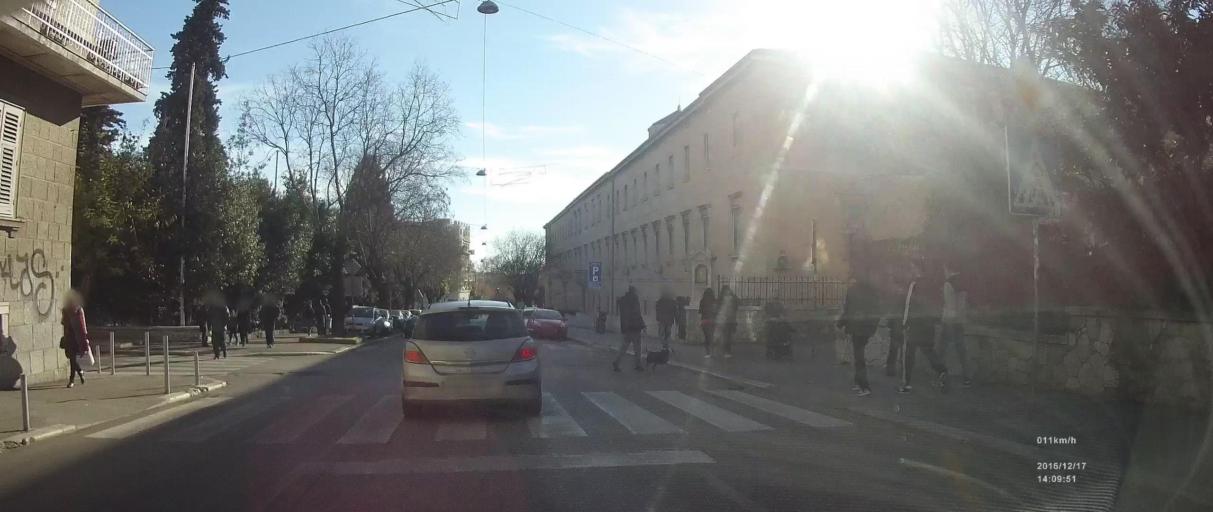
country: HR
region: Splitsko-Dalmatinska
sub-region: Grad Split
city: Split
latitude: 43.5149
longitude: 16.4356
